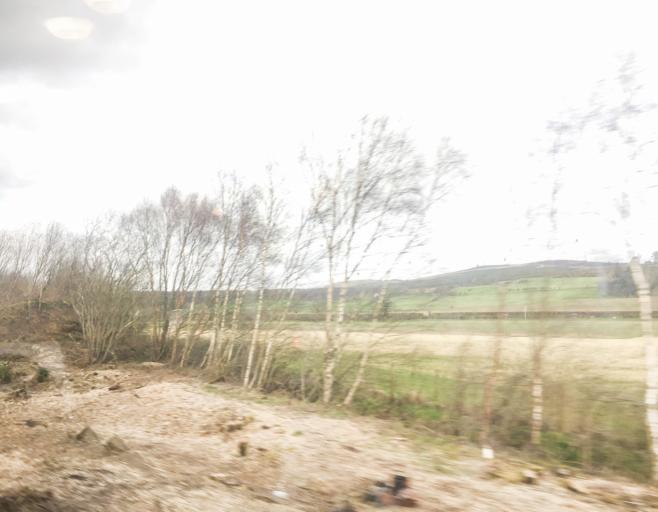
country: GB
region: Scotland
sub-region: Inverclyde
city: Port Glasgow
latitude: 55.9792
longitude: -4.6872
